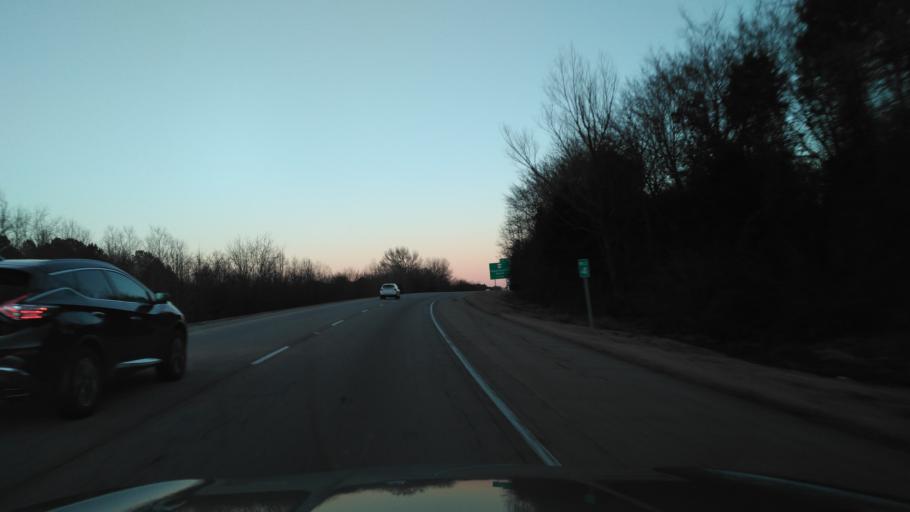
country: US
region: Arkansas
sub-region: Crawford County
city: Van Buren
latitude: 35.4655
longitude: -94.3790
